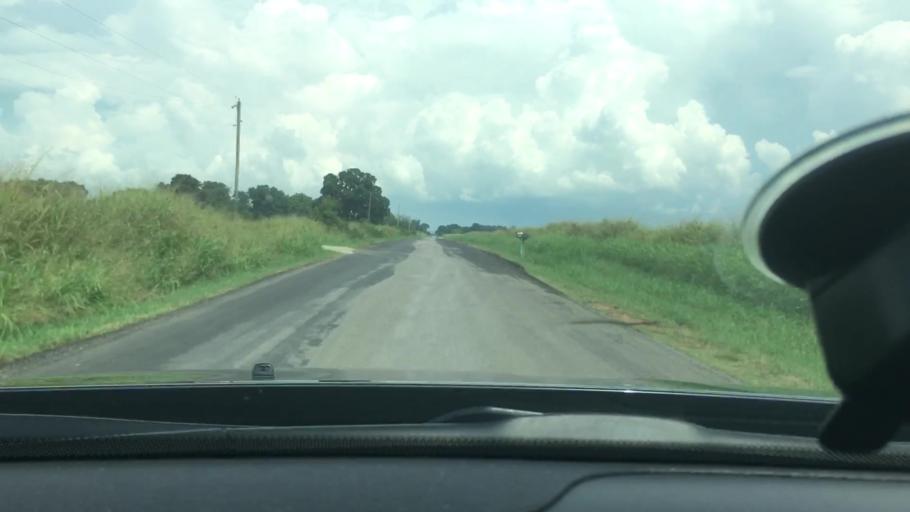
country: US
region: Oklahoma
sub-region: Carter County
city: Dickson
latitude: 34.2048
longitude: -96.8982
